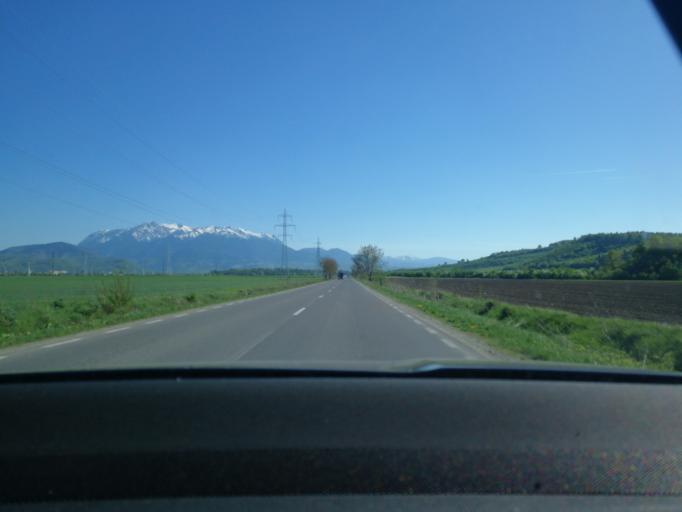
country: RO
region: Brasov
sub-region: Comuna Vulcan
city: Vulcan
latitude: 45.6179
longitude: 25.4246
